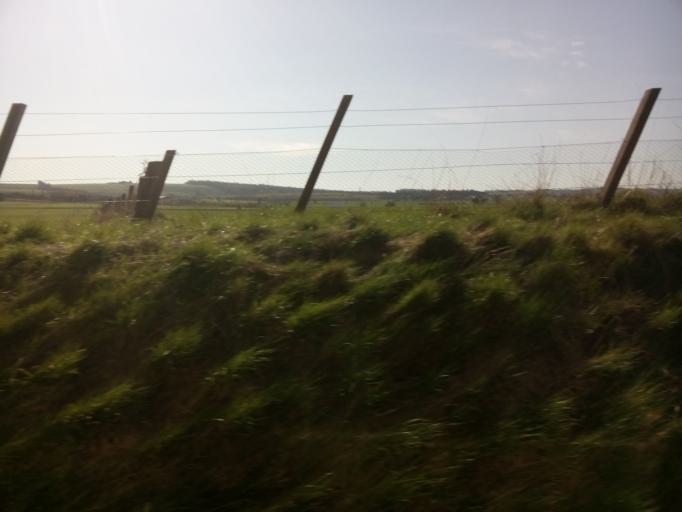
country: GB
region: Scotland
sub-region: East Lothian
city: Musselburgh
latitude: 55.9336
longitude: -3.0357
